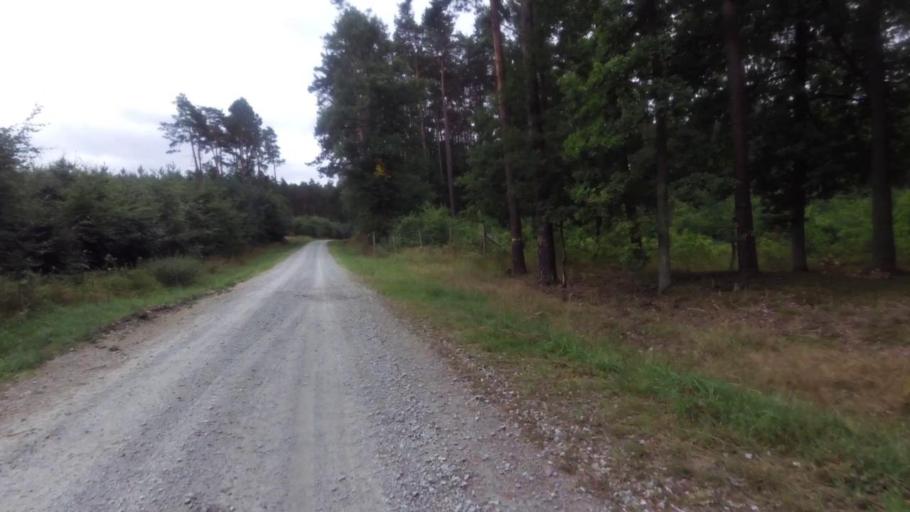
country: PL
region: Lubusz
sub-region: Powiat gorzowski
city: Kostrzyn nad Odra
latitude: 52.6466
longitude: 14.6417
